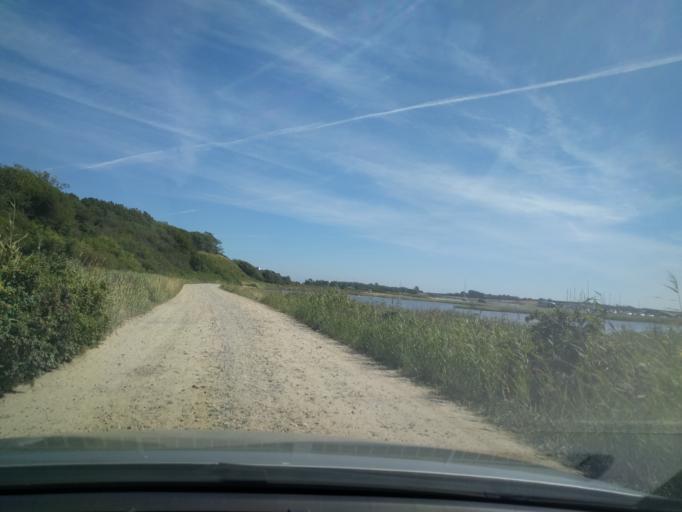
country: DK
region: South Denmark
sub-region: Kerteminde Kommune
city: Munkebo
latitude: 55.6075
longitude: 10.6040
